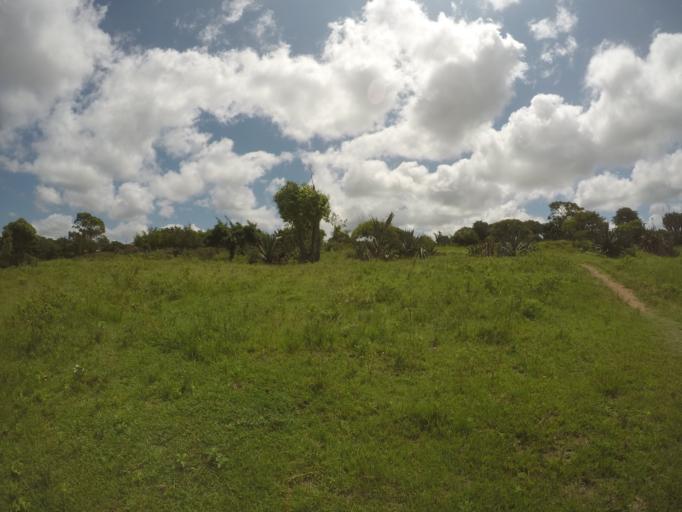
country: ZA
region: KwaZulu-Natal
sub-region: uThungulu District Municipality
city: Empangeni
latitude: -28.5796
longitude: 31.8433
